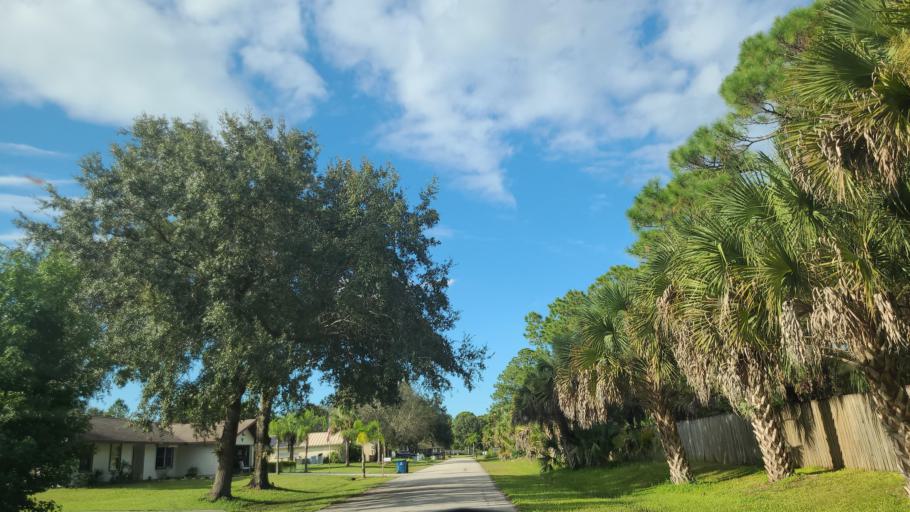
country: US
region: Florida
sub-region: Brevard County
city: June Park
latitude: 28.0006
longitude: -80.6949
